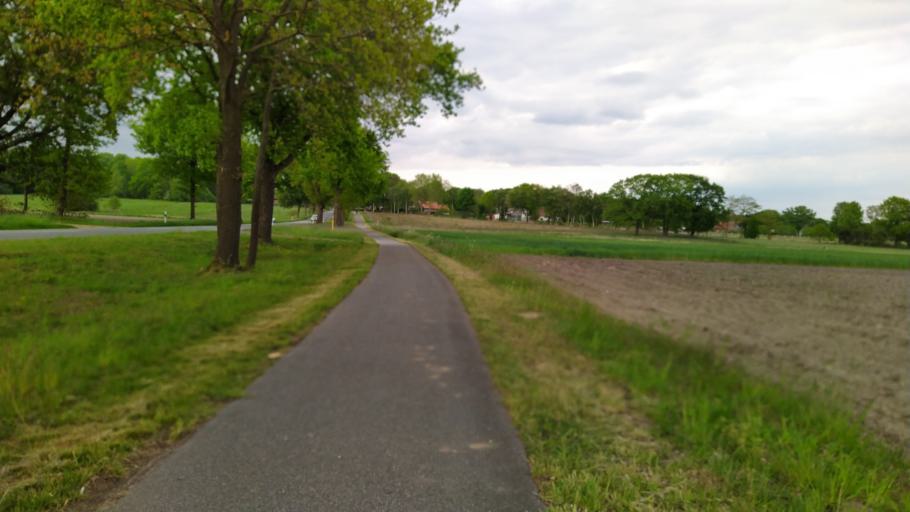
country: DE
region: Lower Saxony
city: Kirchtimke
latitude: 53.2460
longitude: 9.1447
